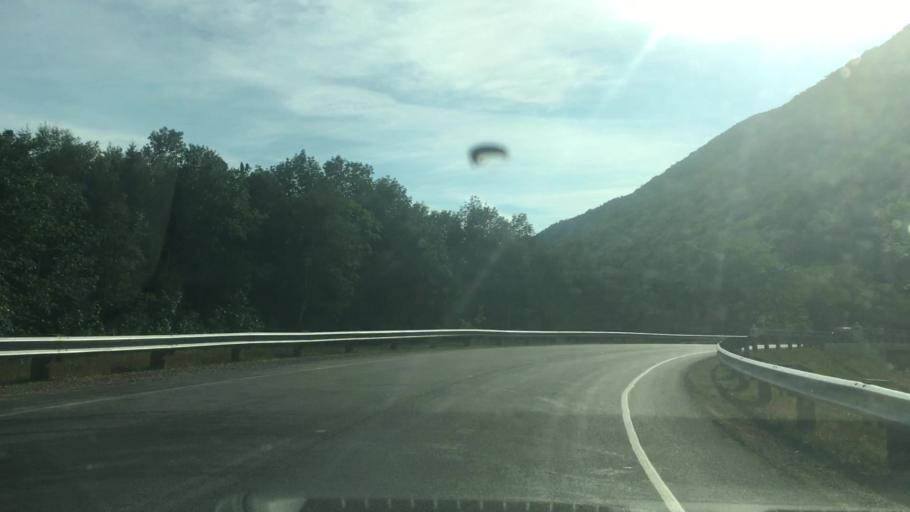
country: CA
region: Nova Scotia
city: Sydney Mines
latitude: 46.8281
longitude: -60.6181
